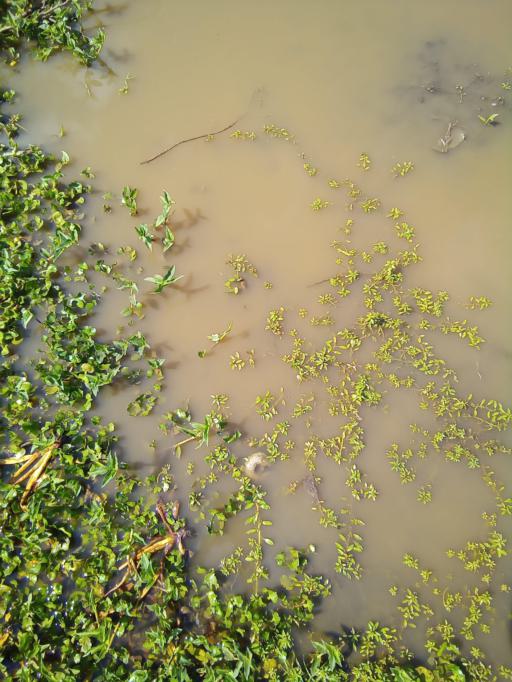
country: KE
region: Homa Bay
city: Homa Bay
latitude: -0.4653
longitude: 34.1824
